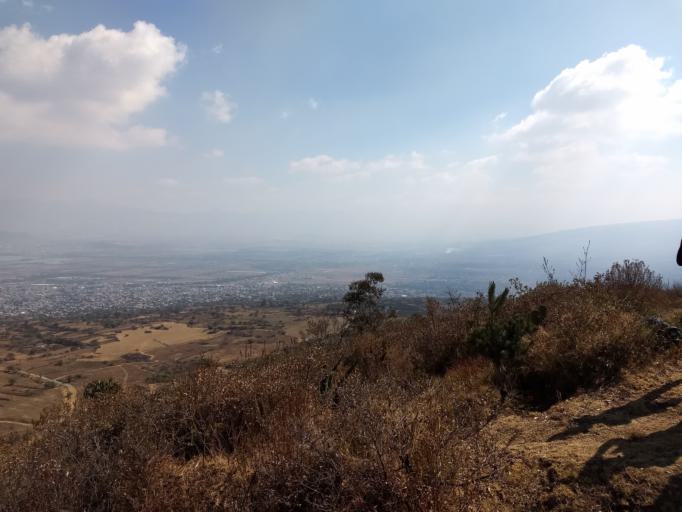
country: MX
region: Mexico City
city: Milpa Alta
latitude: 19.2251
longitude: -99.0295
